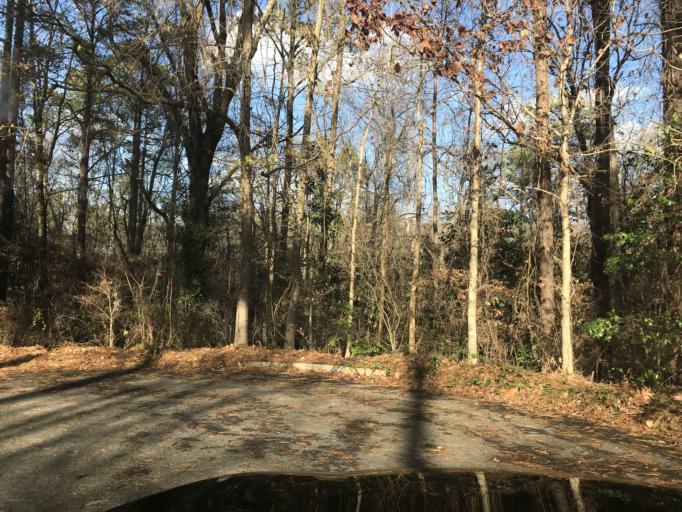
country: US
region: Georgia
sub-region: Fulton County
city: College Park
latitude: 33.6448
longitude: -84.4746
